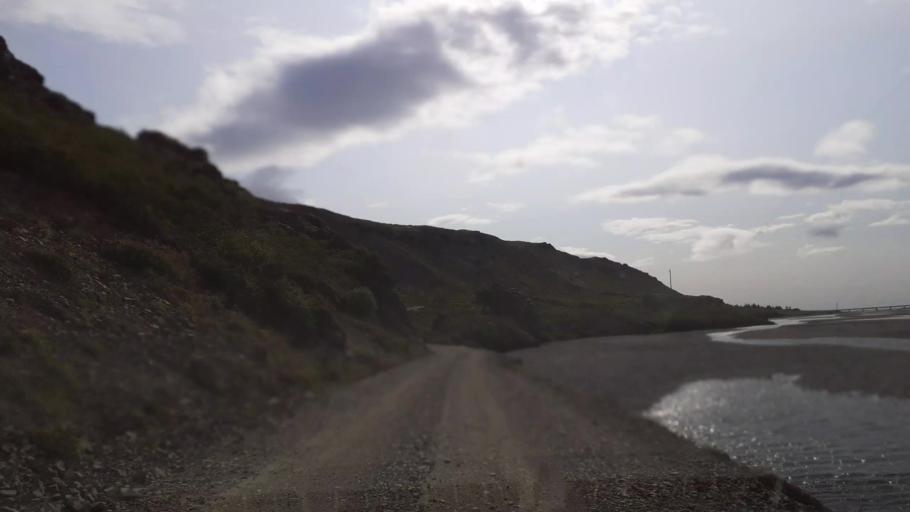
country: IS
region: East
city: Hoefn
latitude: 64.4314
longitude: -14.8907
